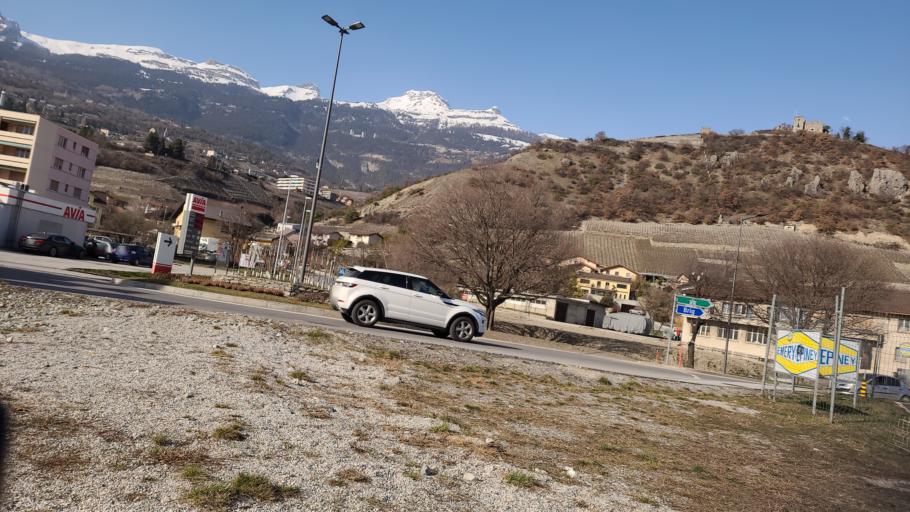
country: CH
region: Valais
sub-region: Sierre District
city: Veyras
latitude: 46.2970
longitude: 7.5447
